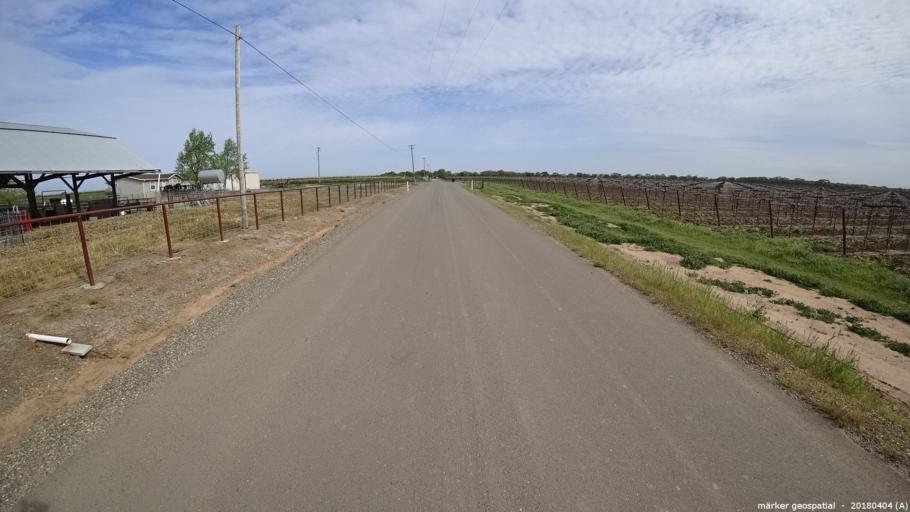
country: US
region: California
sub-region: Sacramento County
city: Herald
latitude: 38.3060
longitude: -121.2772
